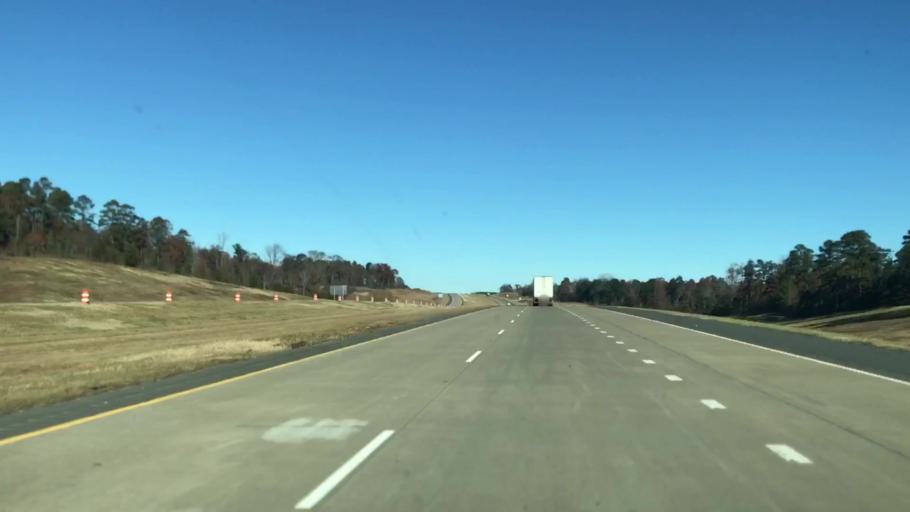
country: US
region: Louisiana
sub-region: Caddo Parish
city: Vivian
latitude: 32.9482
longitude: -93.8985
